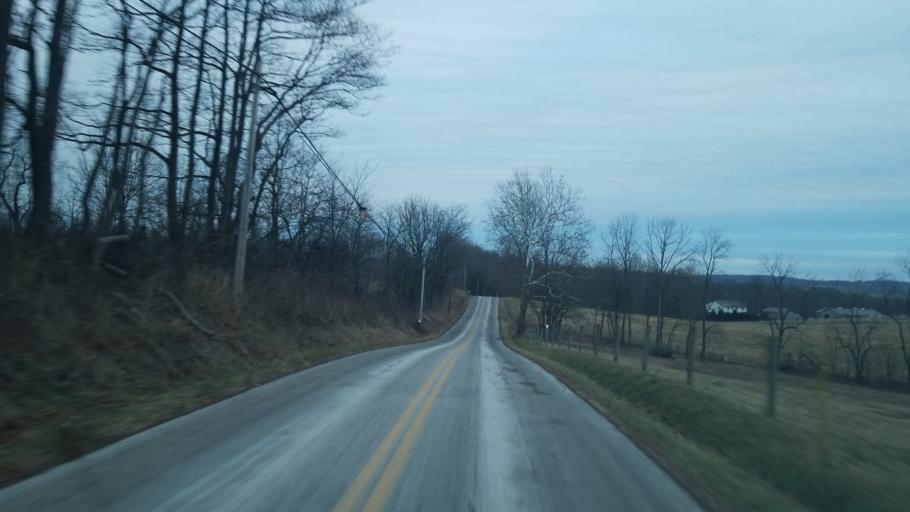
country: US
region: Ohio
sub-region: Holmes County
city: Millersburg
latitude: 40.4897
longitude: -81.8769
